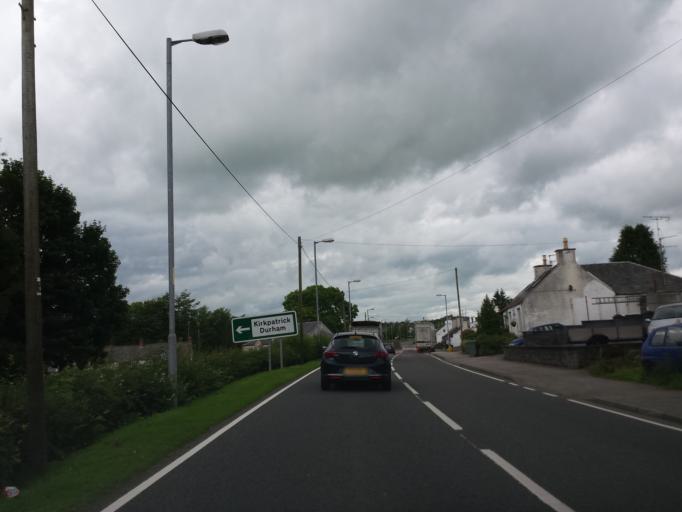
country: GB
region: Scotland
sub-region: Dumfries and Galloway
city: Dalbeattie
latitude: 55.0094
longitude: -3.8680
